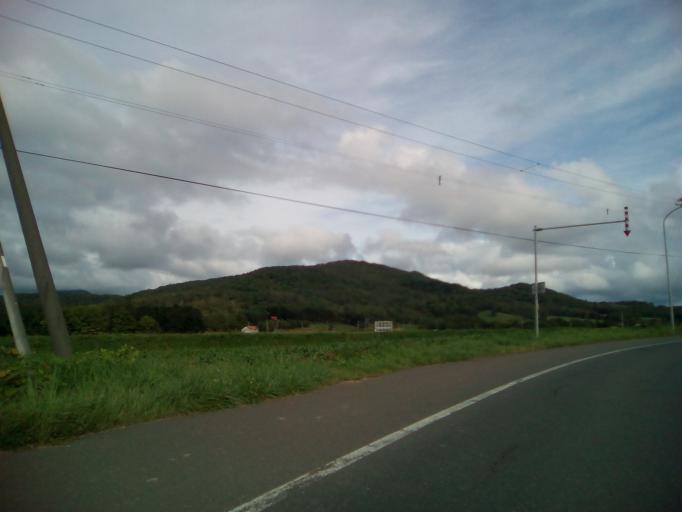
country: JP
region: Hokkaido
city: Niseko Town
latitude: 42.6788
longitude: 140.8409
